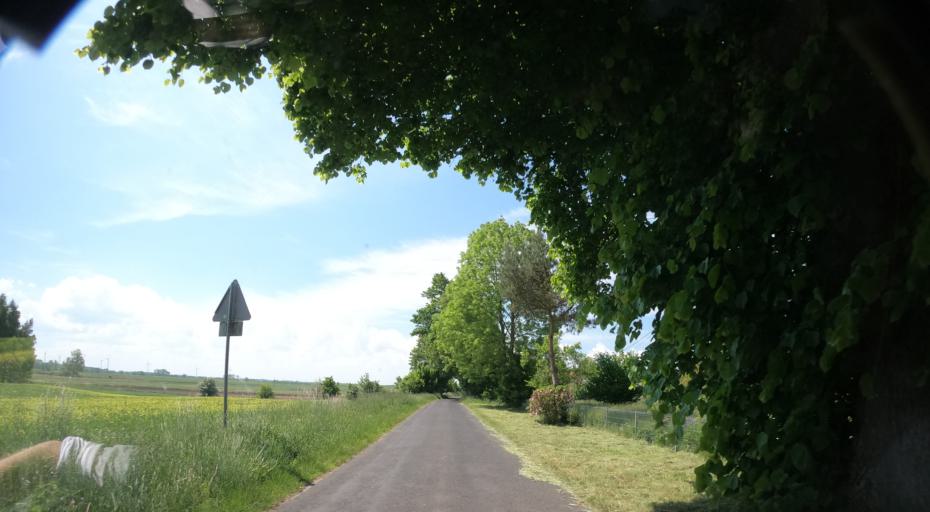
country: PL
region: West Pomeranian Voivodeship
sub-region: Powiat kolobrzeski
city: Ustronie Morskie
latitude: 54.1571
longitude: 15.8032
